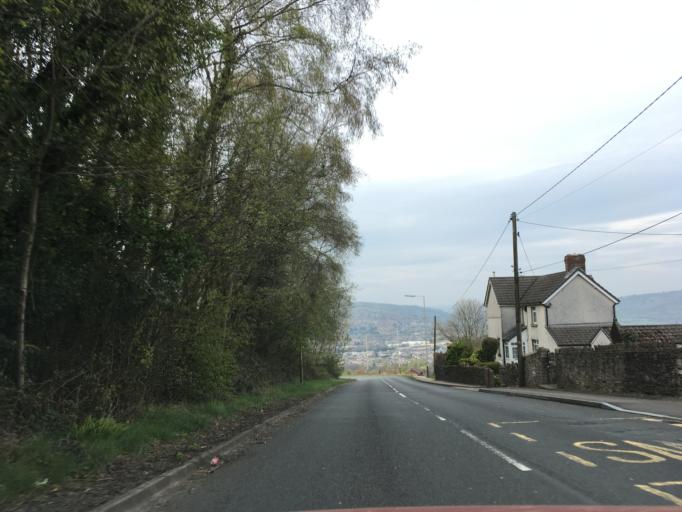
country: GB
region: Wales
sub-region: Caerphilly County Borough
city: Caerphilly
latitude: 51.5626
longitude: -3.2307
